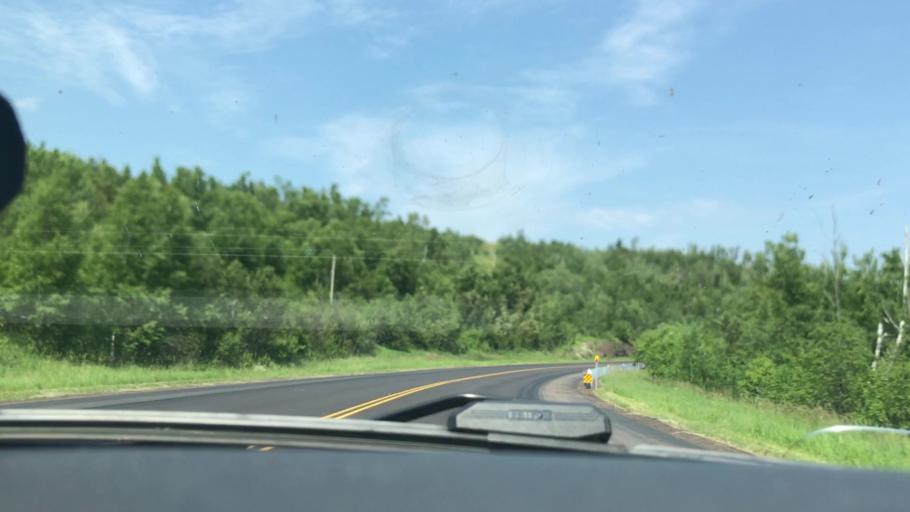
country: US
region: Minnesota
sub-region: Lake County
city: Silver Bay
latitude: 47.3662
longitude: -91.1720
